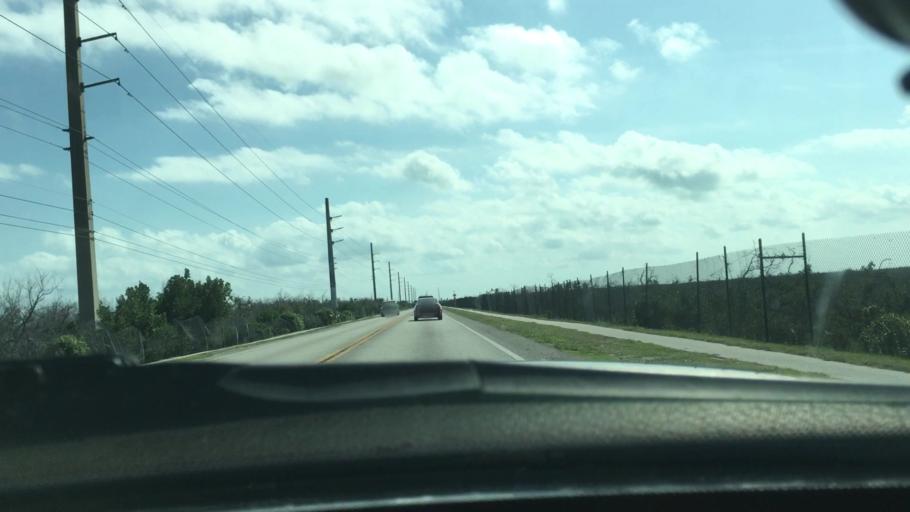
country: US
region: Florida
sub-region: Monroe County
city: Big Pine Key
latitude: 24.6611
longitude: -81.3385
